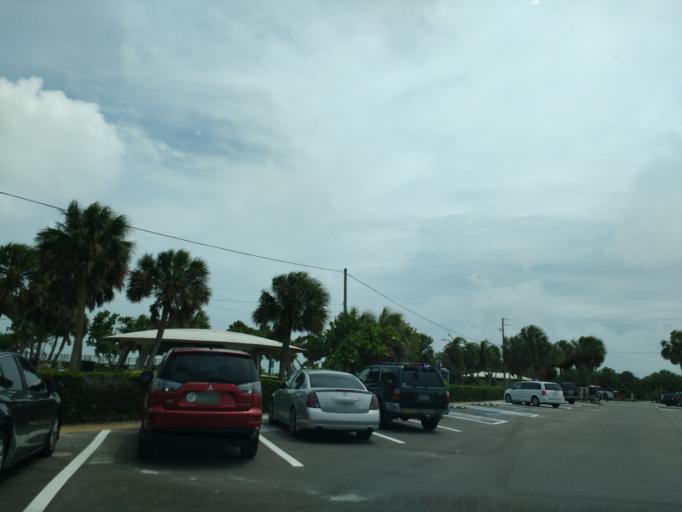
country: US
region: Florida
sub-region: Pinellas County
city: Tierra Verde
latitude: 27.6174
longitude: -82.7261
